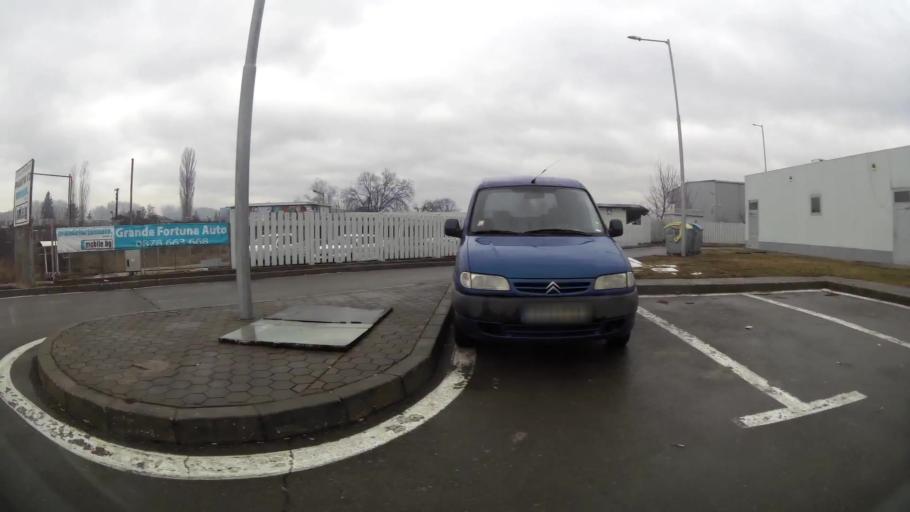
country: BG
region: Sofia-Capital
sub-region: Stolichna Obshtina
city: Sofia
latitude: 42.7095
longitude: 23.4277
